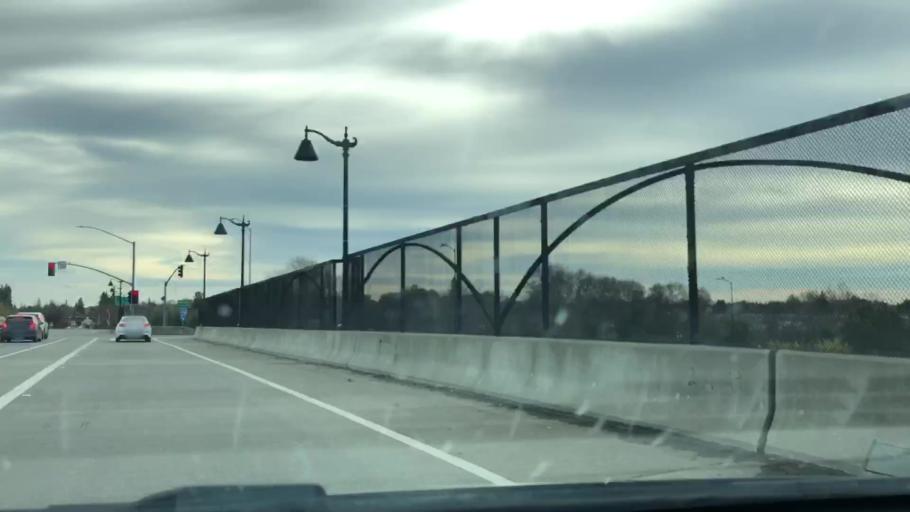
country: US
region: California
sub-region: Yolo County
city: Davis
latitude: 38.5539
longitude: -121.6952
